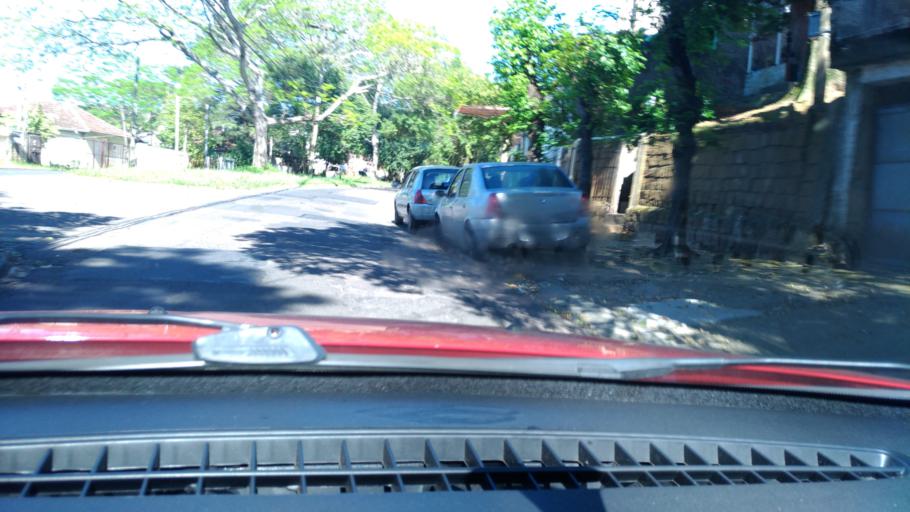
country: BR
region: Rio Grande do Sul
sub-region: Cachoeirinha
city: Cachoeirinha
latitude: -30.0330
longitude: -51.1299
